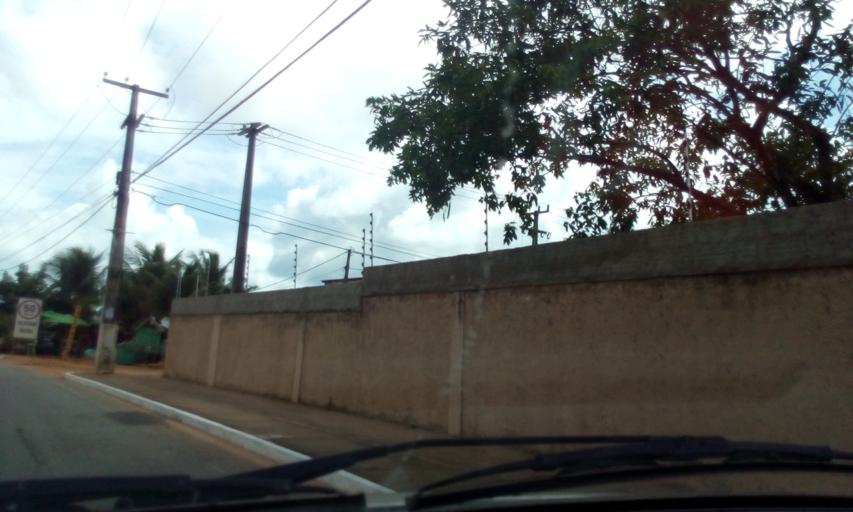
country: BR
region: Rio Grande do Norte
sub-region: Parnamirim
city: Parnamirim
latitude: -5.8945
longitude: -35.1938
